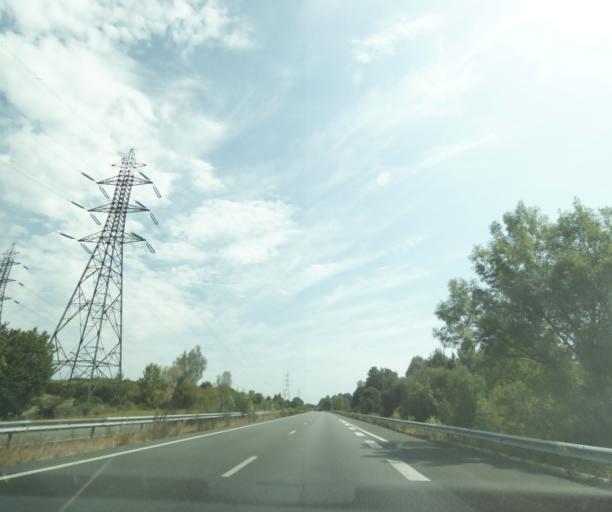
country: FR
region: Aquitaine
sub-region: Departement de la Gironde
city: Pugnac
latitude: 45.1025
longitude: -0.4800
